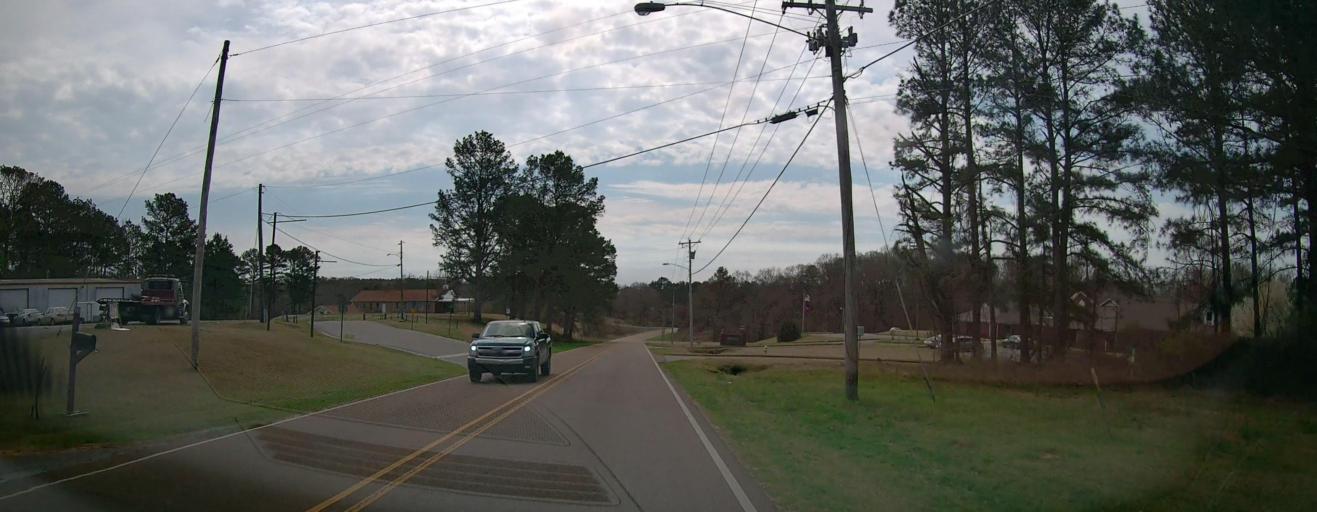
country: US
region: Mississippi
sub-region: Marshall County
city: Holly Springs
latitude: 34.7608
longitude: -89.4301
